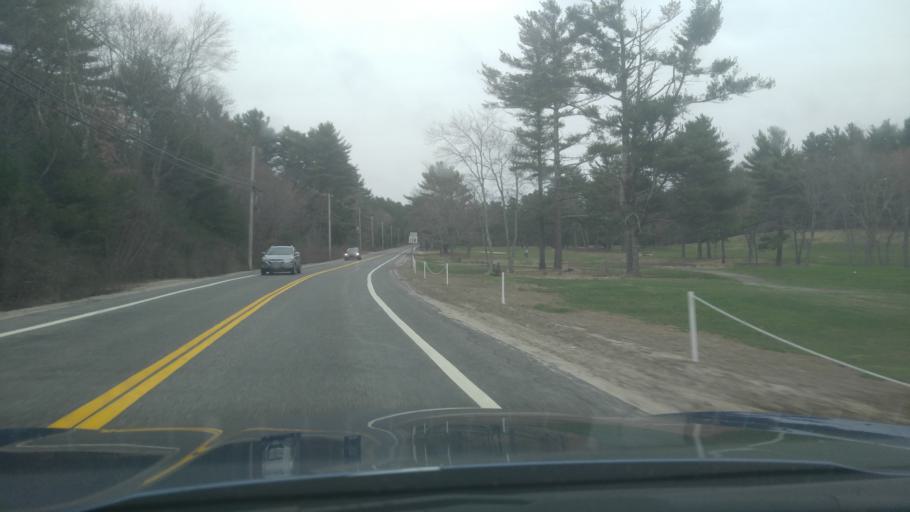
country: US
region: Rhode Island
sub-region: Kent County
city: West Greenwich
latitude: 41.6712
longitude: -71.6301
